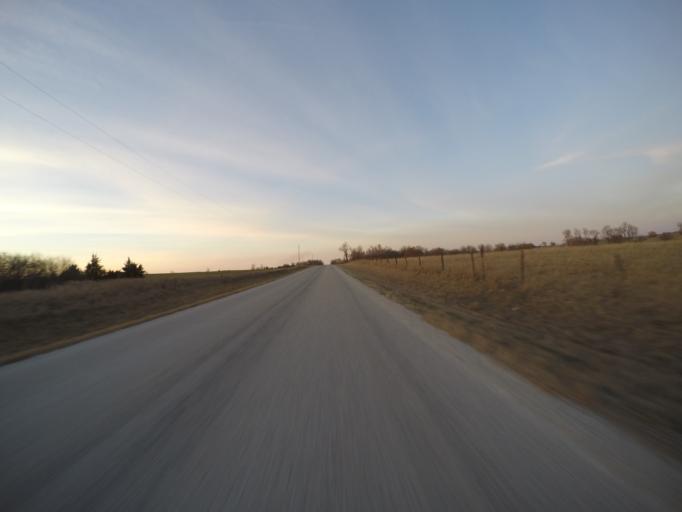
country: US
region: Kansas
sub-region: Washington County
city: Washington
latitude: 39.5830
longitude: -96.9942
